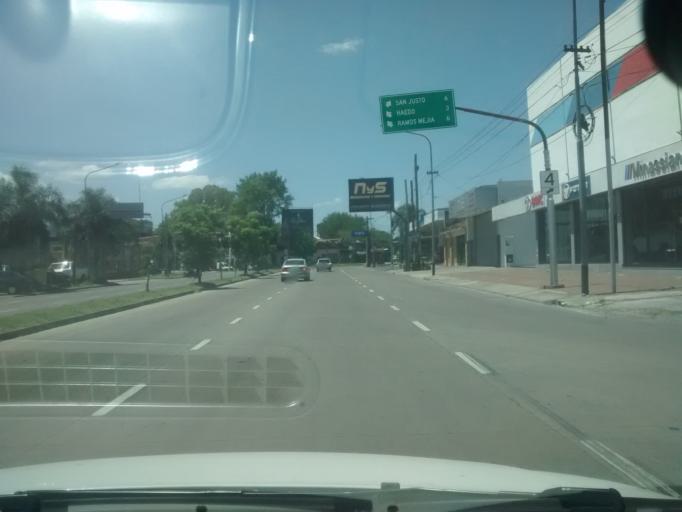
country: AR
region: Buenos Aires
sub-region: Partido de Moron
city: Moron
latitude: -34.6604
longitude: -58.6087
